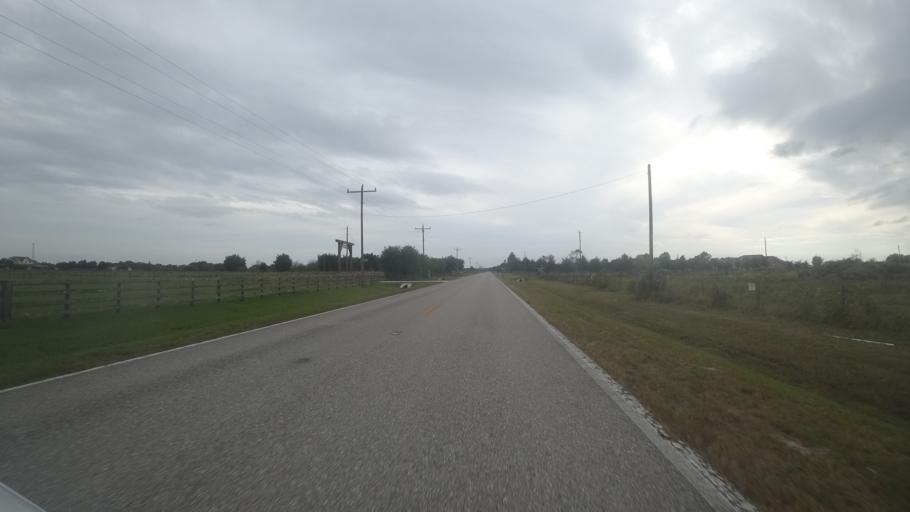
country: US
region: Florida
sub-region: Sarasota County
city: Warm Mineral Springs
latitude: 27.2836
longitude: -82.1936
